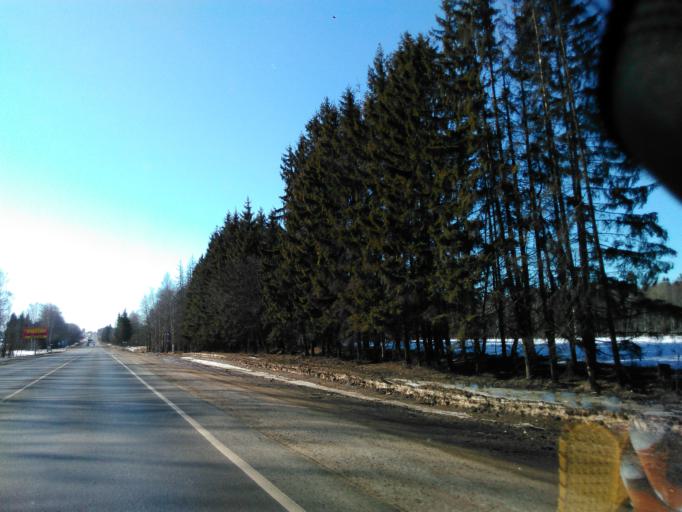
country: RU
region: Moskovskaya
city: Yermolino
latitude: 56.1364
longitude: 37.4417
